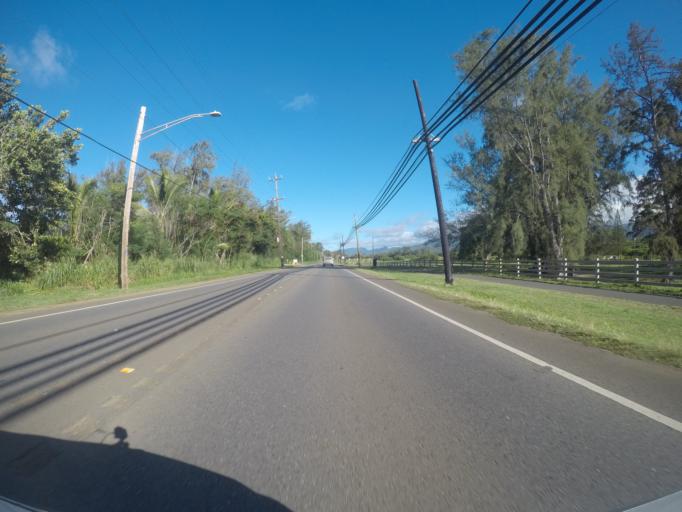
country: US
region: Hawaii
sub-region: Honolulu County
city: La'ie
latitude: 21.6630
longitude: -157.9353
